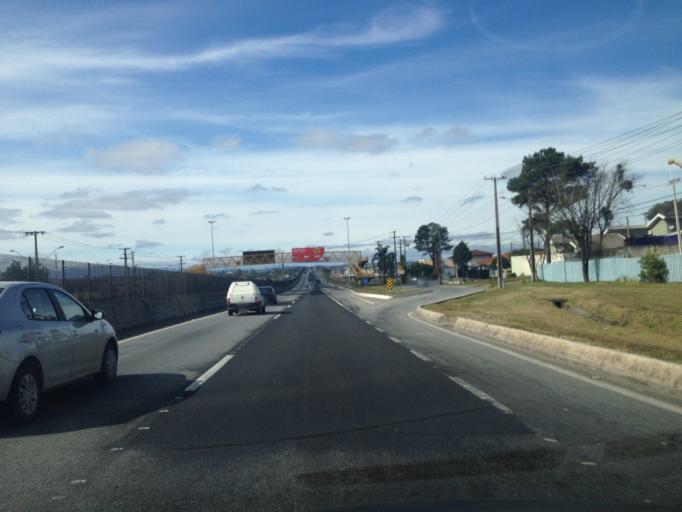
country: BR
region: Parana
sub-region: Pinhais
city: Pinhais
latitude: -25.4776
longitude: -49.2044
